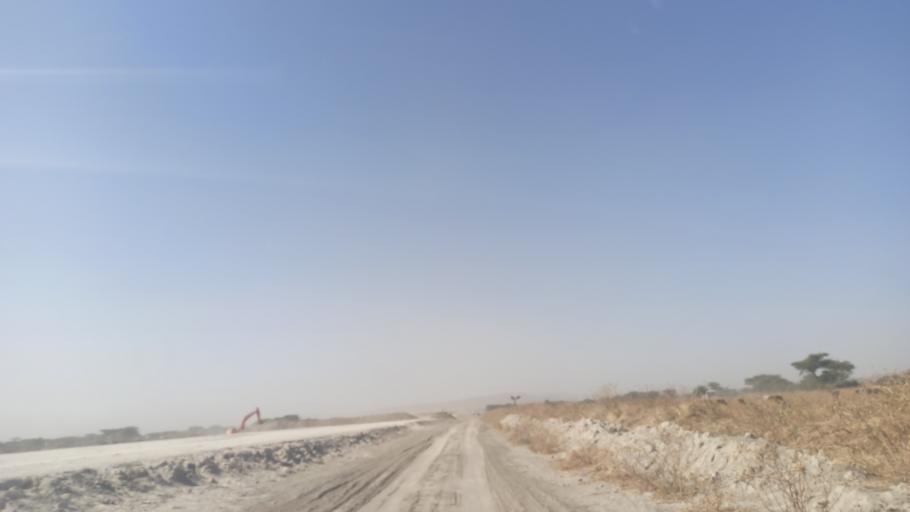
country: ET
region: Oromiya
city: Ziway
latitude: 7.7328
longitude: 38.6248
